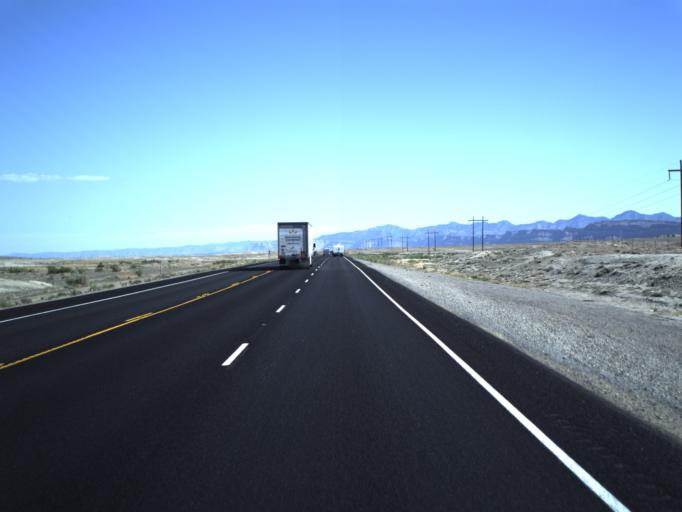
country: US
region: Utah
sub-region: Carbon County
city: East Carbon City
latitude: 39.1674
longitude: -110.3382
